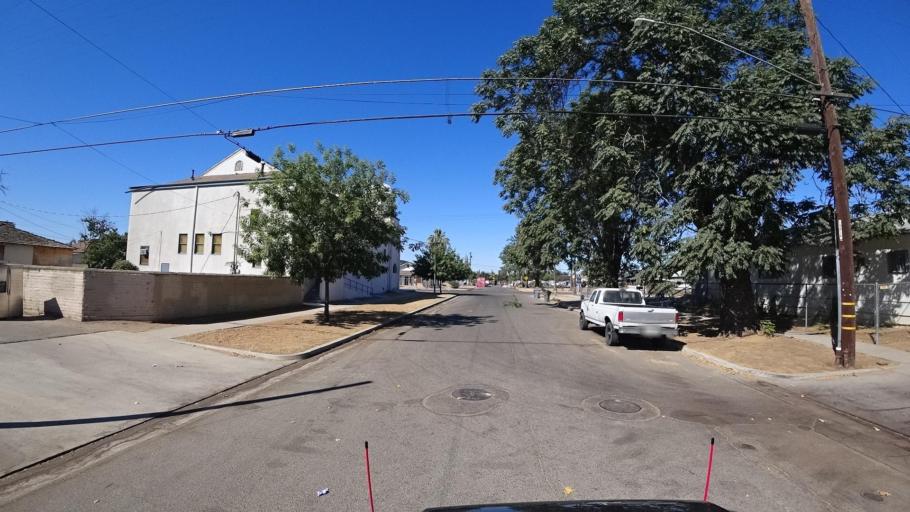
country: US
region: California
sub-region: Fresno County
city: Fresno
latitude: 36.7232
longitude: -119.7878
